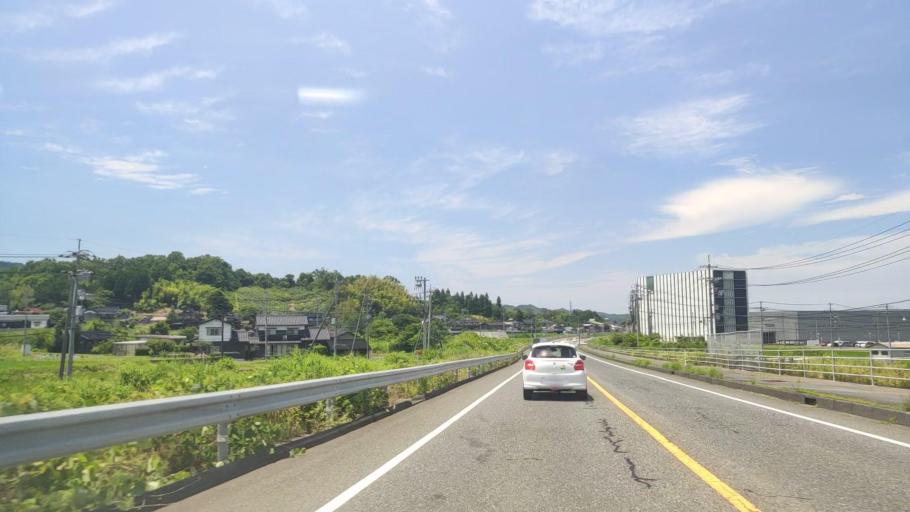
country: JP
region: Tottori
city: Tottori
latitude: 35.4501
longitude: 134.2505
